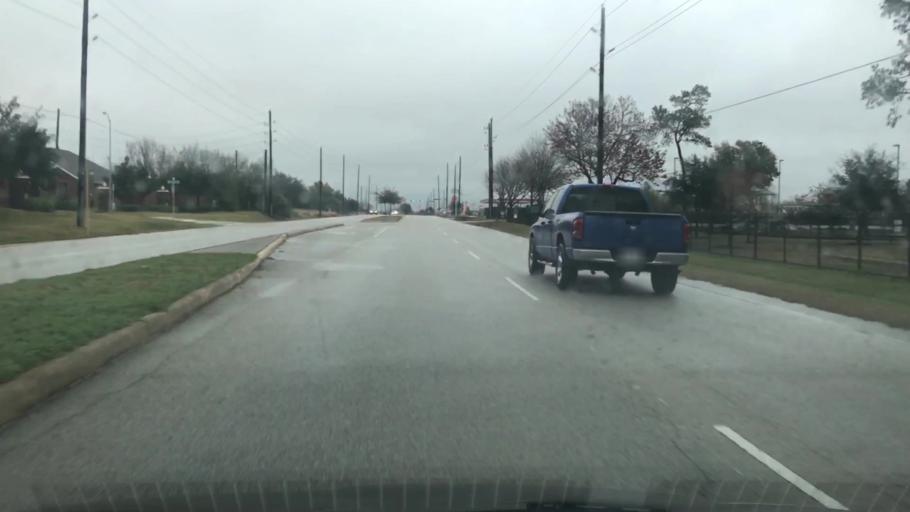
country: US
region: Texas
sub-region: Harris County
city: Katy
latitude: 29.8317
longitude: -95.7490
